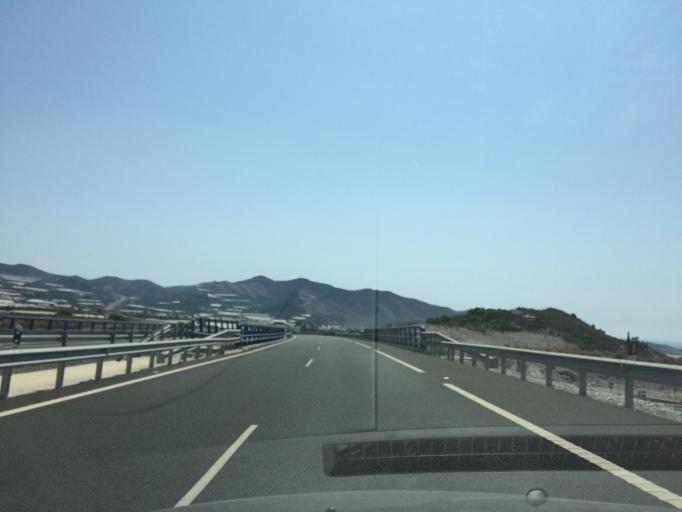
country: ES
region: Andalusia
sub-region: Provincia de Granada
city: Motril
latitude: 36.7403
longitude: -3.4866
